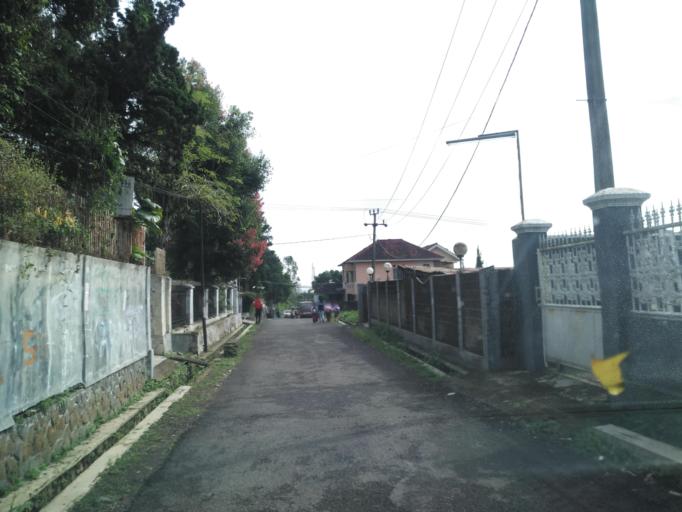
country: ID
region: West Java
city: Sukabumi
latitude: -6.7520
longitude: 107.0484
